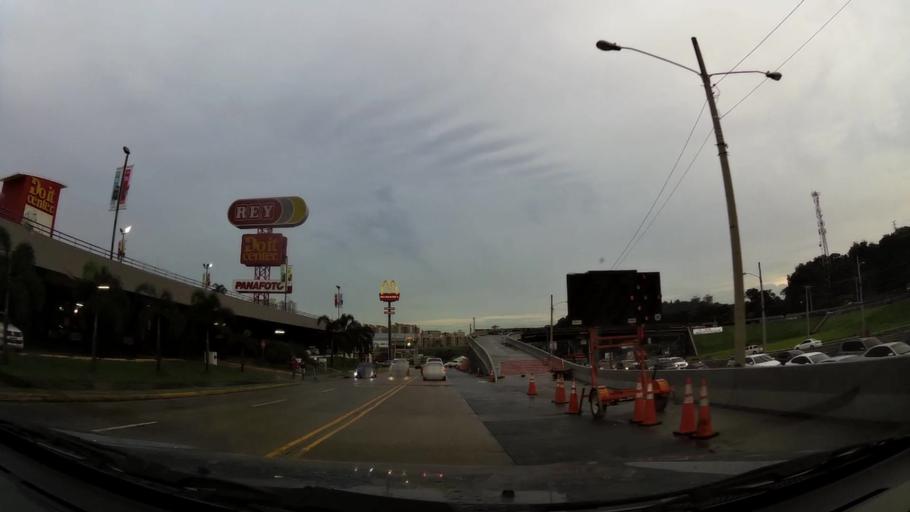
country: PA
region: Panama
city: Panama
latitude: 9.0302
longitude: -79.5321
